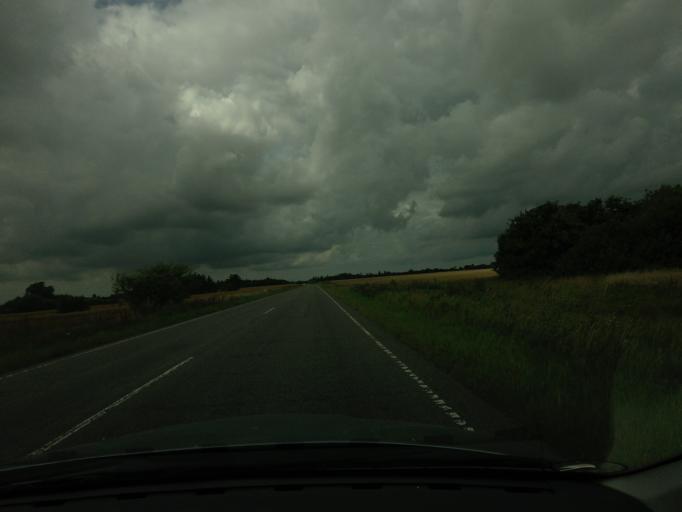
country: DK
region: North Denmark
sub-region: Hjorring Kommune
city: Hjorring
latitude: 57.4234
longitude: 10.0073
